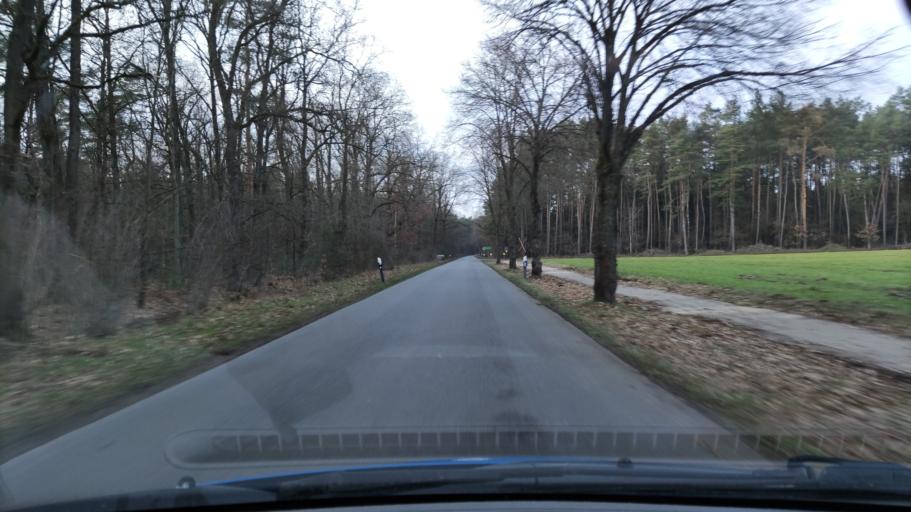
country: DE
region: Lower Saxony
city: Gerdau
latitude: 52.9374
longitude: 10.4355
